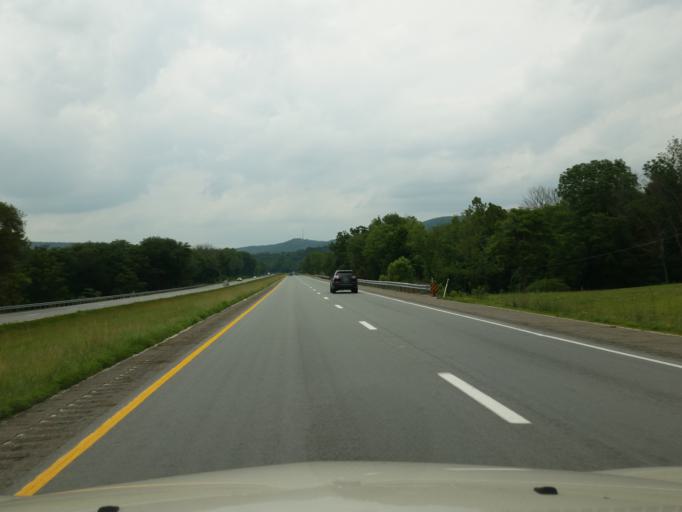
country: US
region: Pennsylvania
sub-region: Perry County
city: Newport
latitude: 40.5309
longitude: -77.1374
